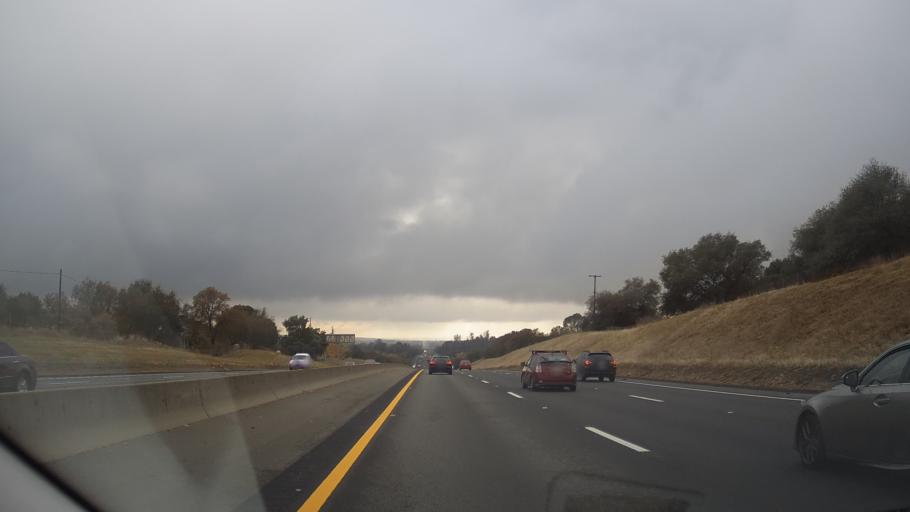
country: US
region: California
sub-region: Placer County
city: Newcastle
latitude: 38.8533
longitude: -121.1454
